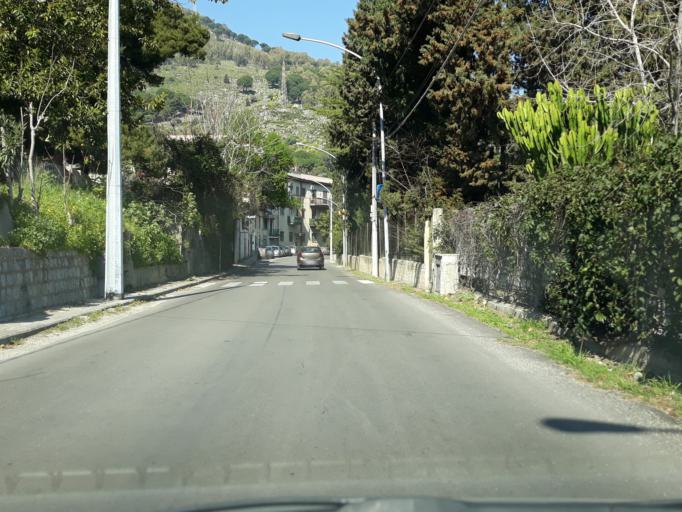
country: IT
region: Sicily
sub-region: Palermo
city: Piano dei Geli
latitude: 38.1164
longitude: 13.2894
